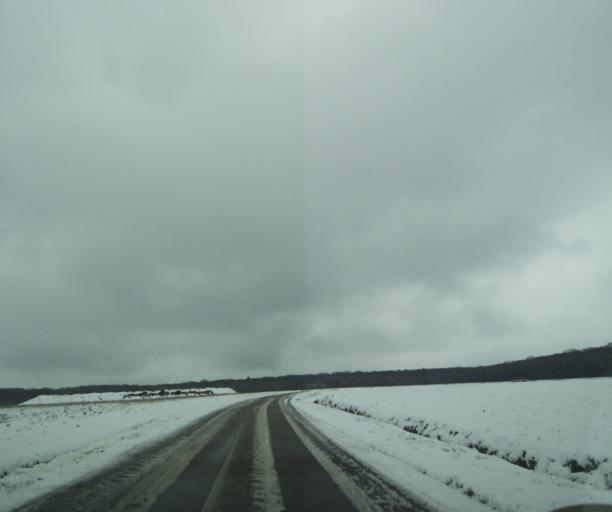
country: FR
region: Champagne-Ardenne
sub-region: Departement de la Haute-Marne
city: Laneuville-a-Remy
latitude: 48.3983
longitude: 4.8617
